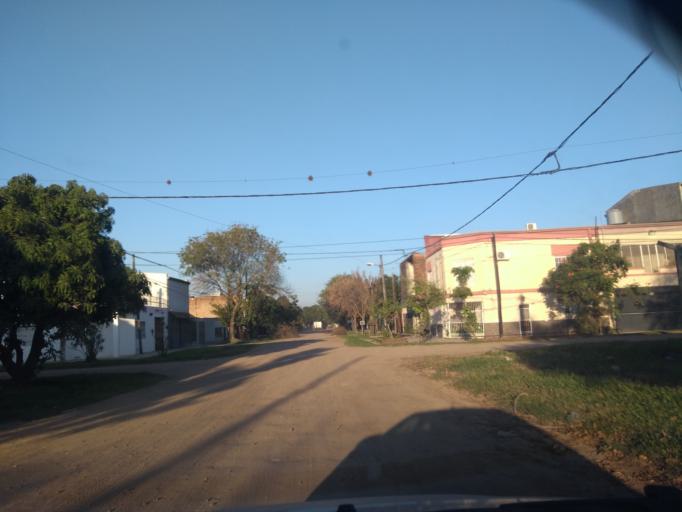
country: AR
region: Chaco
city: Barranqueras
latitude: -27.4768
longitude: -58.9608
